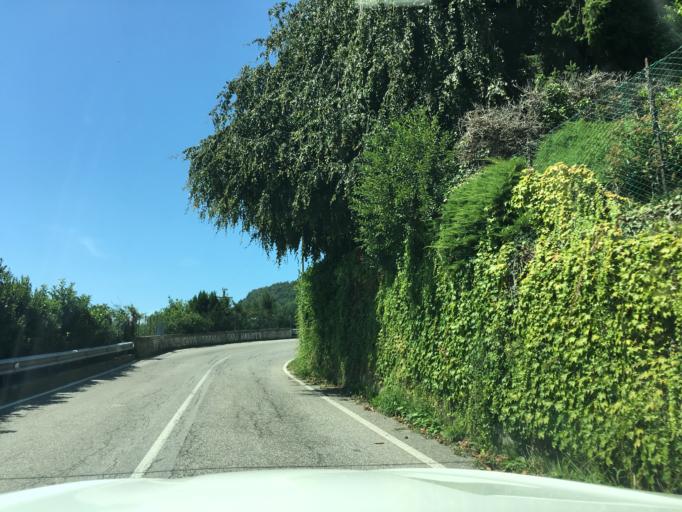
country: IT
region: Lombardy
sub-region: Provincia di Bergamo
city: Nembro
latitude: 45.7460
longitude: 9.7594
